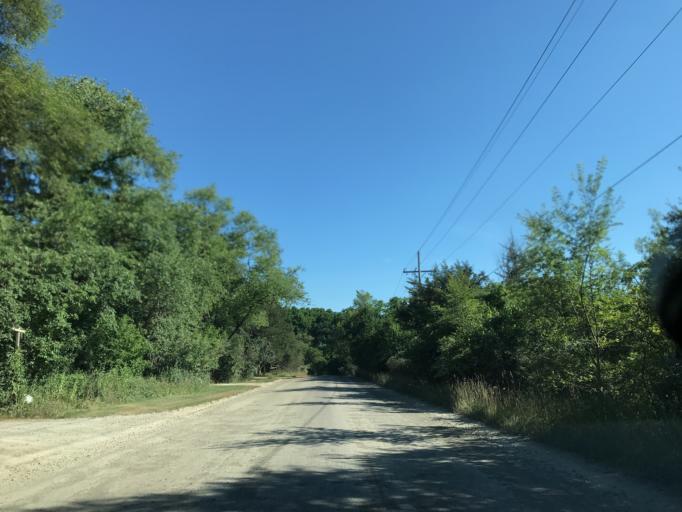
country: US
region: Michigan
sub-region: Washtenaw County
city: Ypsilanti
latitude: 42.3029
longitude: -83.6539
